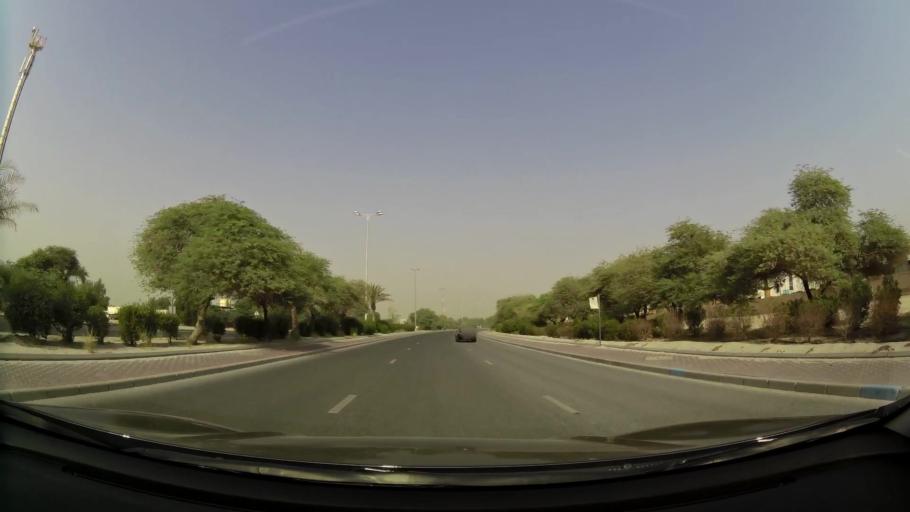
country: KW
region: Al Asimah
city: Ar Rabiyah
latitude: 29.2815
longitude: 47.8355
